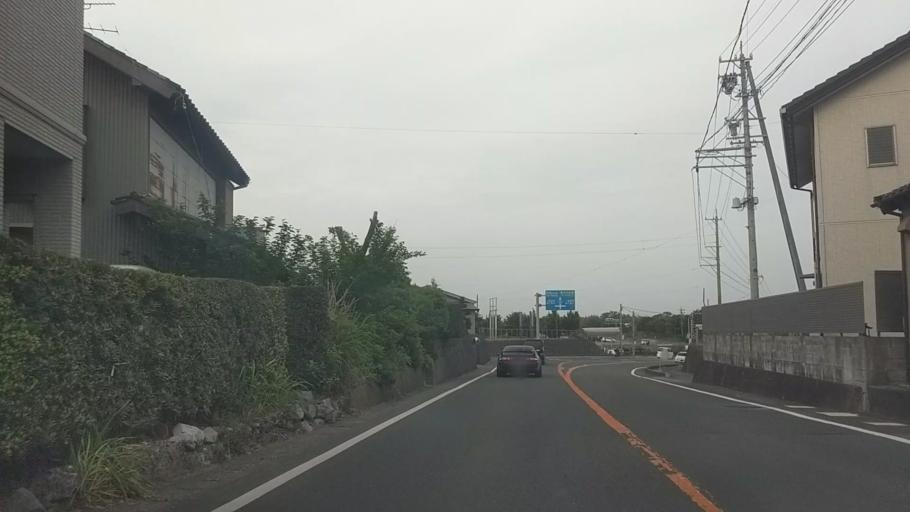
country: JP
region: Shizuoka
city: Hamamatsu
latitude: 34.7643
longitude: 137.6406
